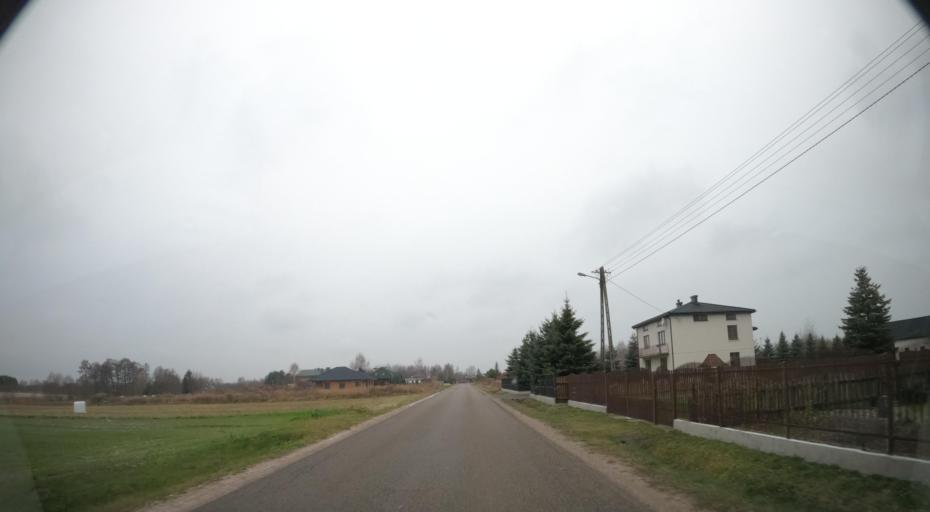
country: PL
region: Masovian Voivodeship
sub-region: Powiat radomski
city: Skaryszew
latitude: 51.3792
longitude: 21.2414
